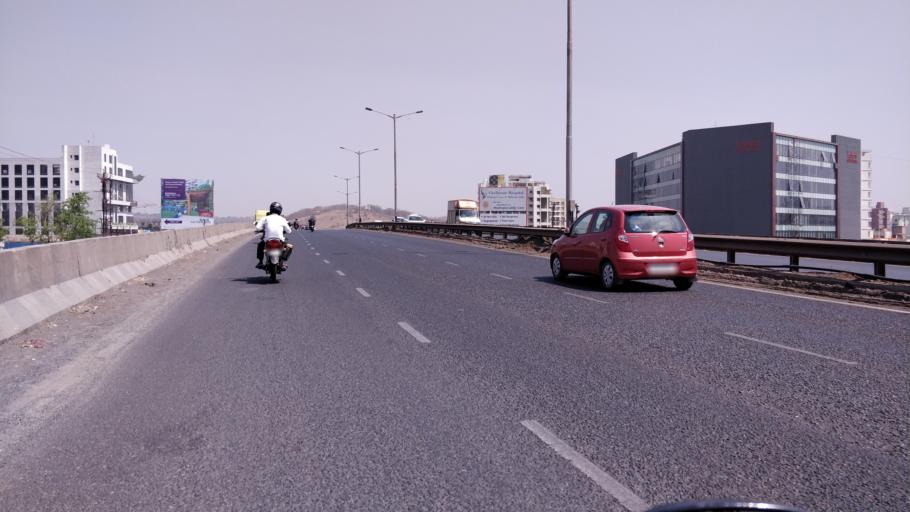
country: IN
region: Maharashtra
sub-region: Pune Division
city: Kharakvasla
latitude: 18.5183
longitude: 73.7687
